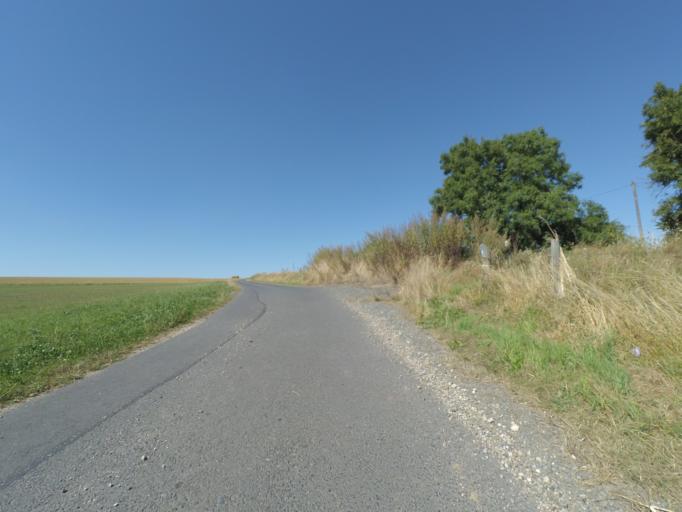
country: DE
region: Rheinland-Pfalz
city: Bad Bertrich
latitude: 50.0955
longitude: 7.0196
